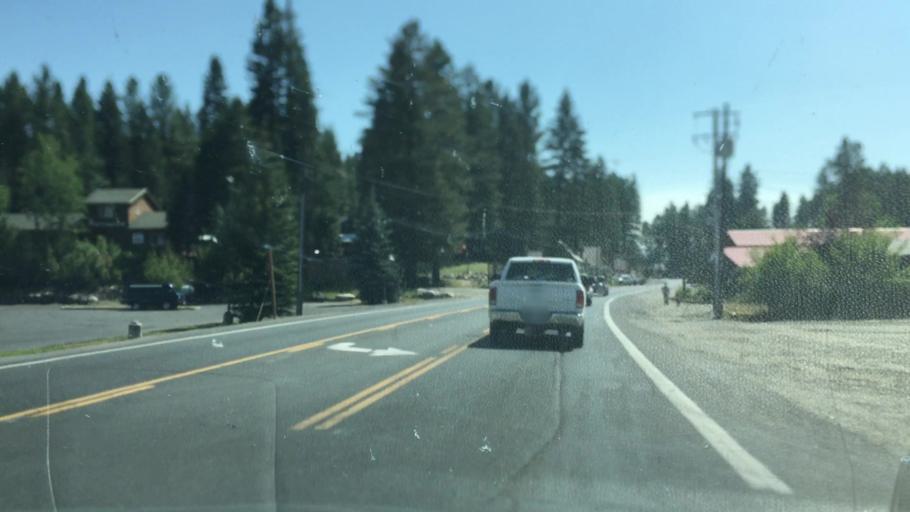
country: US
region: Idaho
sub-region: Valley County
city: McCall
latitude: 44.9059
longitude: -116.0976
